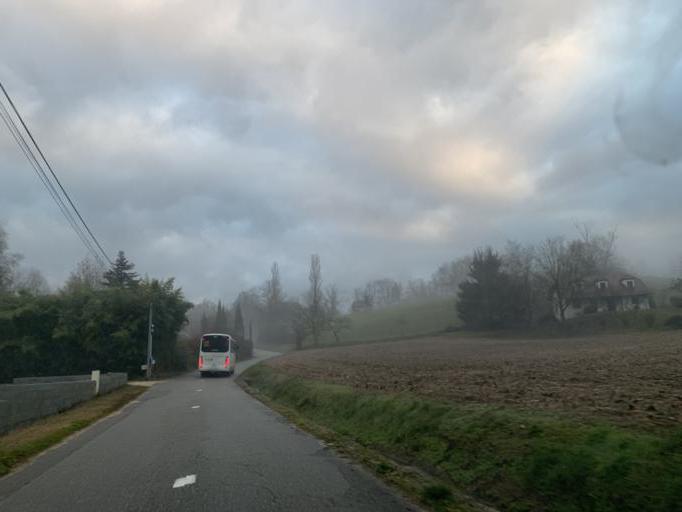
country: FR
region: Rhone-Alpes
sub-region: Departement de l'Ain
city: Belley
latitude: 45.7852
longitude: 5.6903
